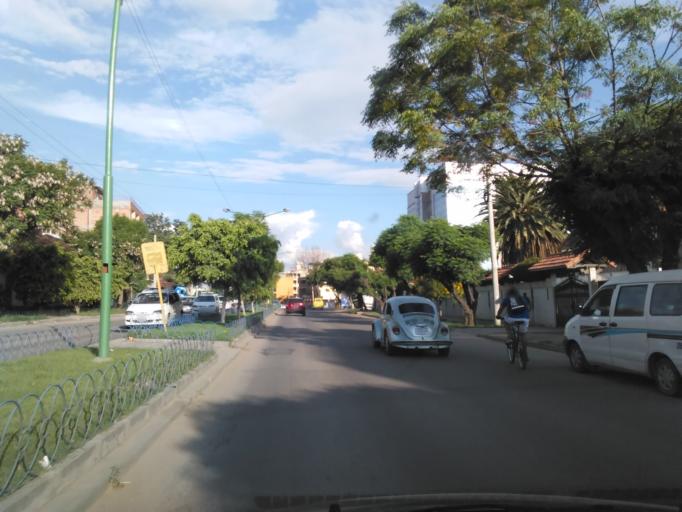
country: BO
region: Cochabamba
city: Cochabamba
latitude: -17.3652
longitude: -66.1762
